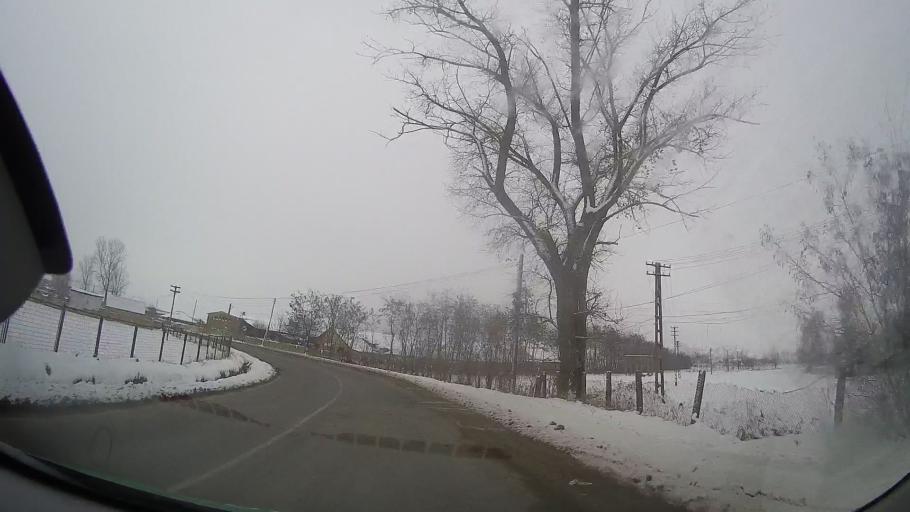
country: RO
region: Vaslui
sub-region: Comuna Todiresti
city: Todiresti
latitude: 46.8390
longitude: 27.3942
